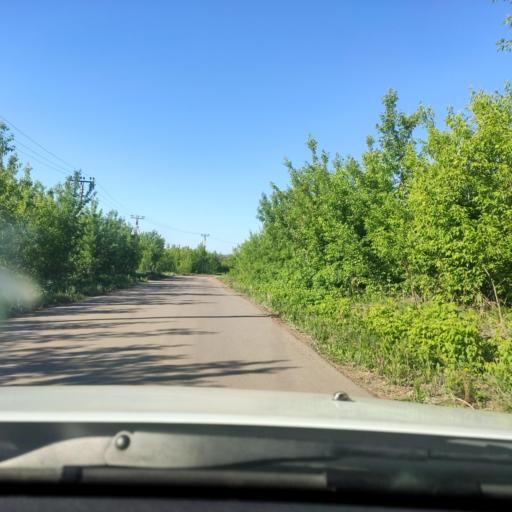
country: RU
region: Bashkortostan
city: Avdon
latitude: 54.6503
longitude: 55.7510
